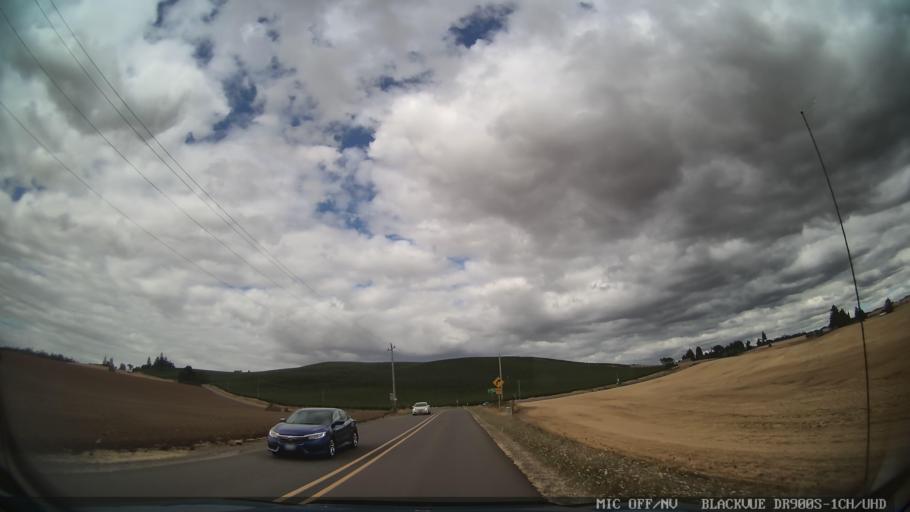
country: US
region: Oregon
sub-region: Marion County
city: Sublimity
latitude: 44.8713
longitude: -122.7352
